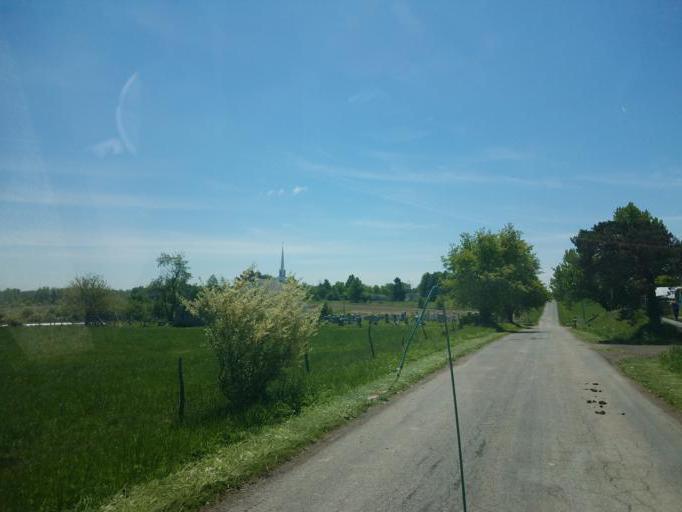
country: US
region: Ohio
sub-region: Wayne County
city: West Salem
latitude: 40.9753
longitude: -82.1771
